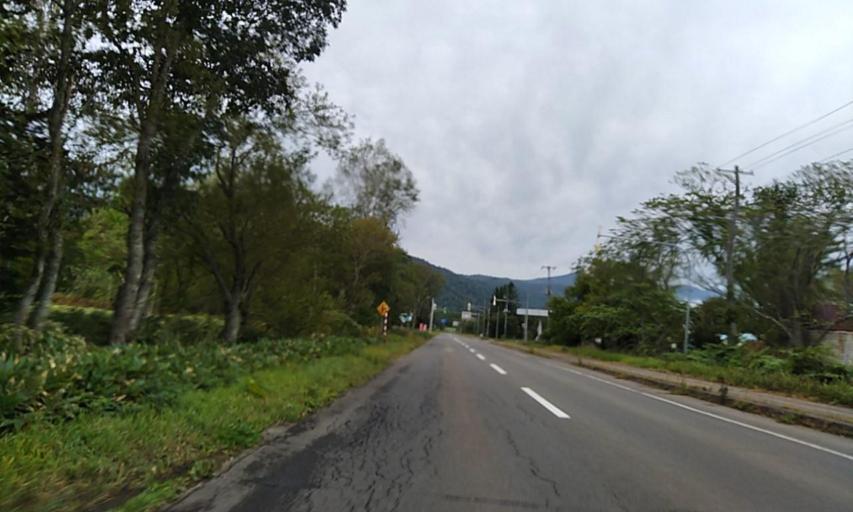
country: JP
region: Hokkaido
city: Bihoro
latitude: 43.5542
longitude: 144.3410
